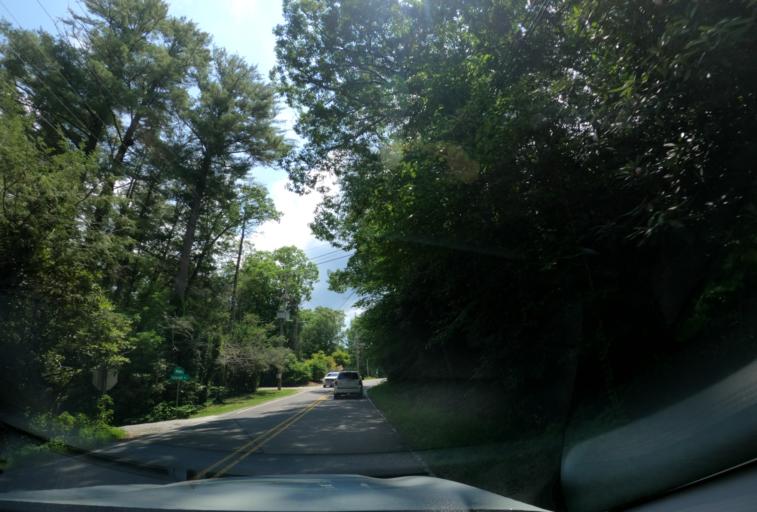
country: US
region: North Carolina
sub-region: Macon County
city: Franklin
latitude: 35.0622
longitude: -83.2105
